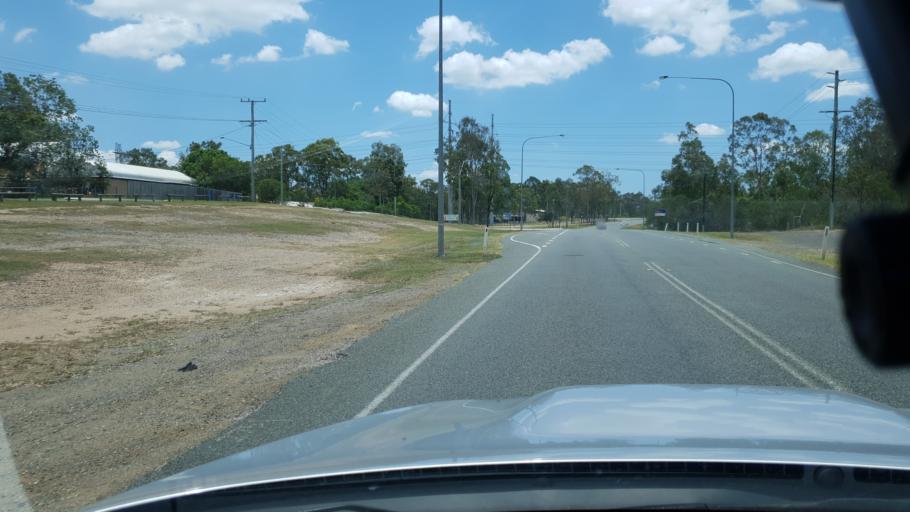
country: AU
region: Queensland
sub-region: Logan
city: North Maclean
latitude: -27.7312
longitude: 152.9844
